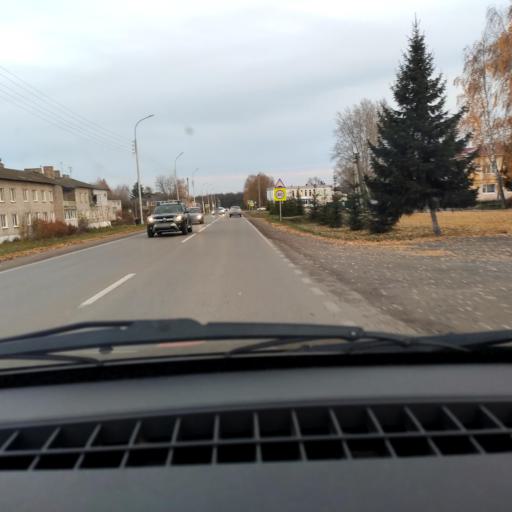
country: RU
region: Bashkortostan
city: Mikhaylovka
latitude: 54.8119
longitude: 55.8071
